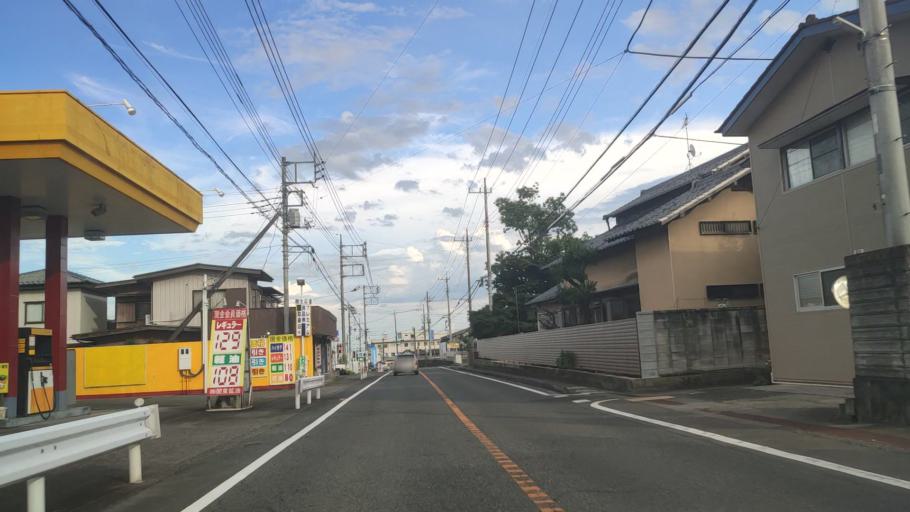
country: JP
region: Gunma
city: Kiryu
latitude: 36.4180
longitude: 139.3080
